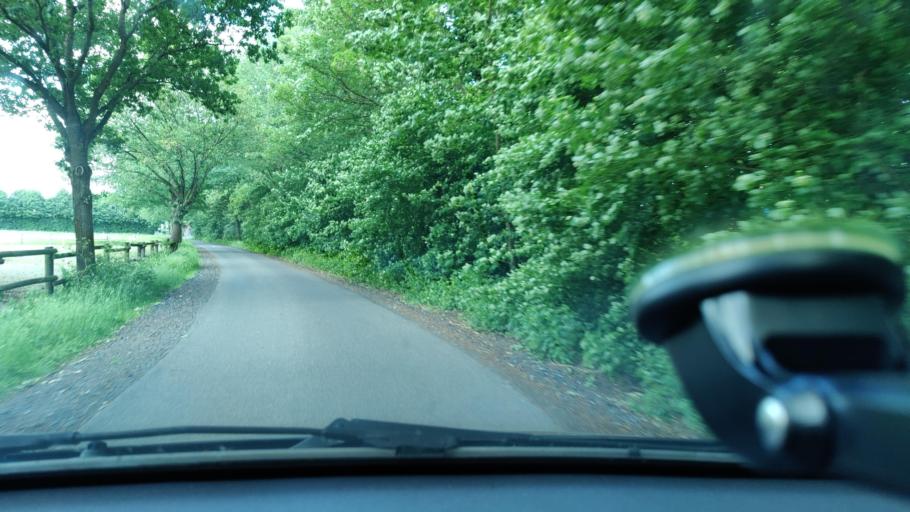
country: DE
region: North Rhine-Westphalia
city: Stadtlohn
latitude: 51.9993
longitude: 6.9253
